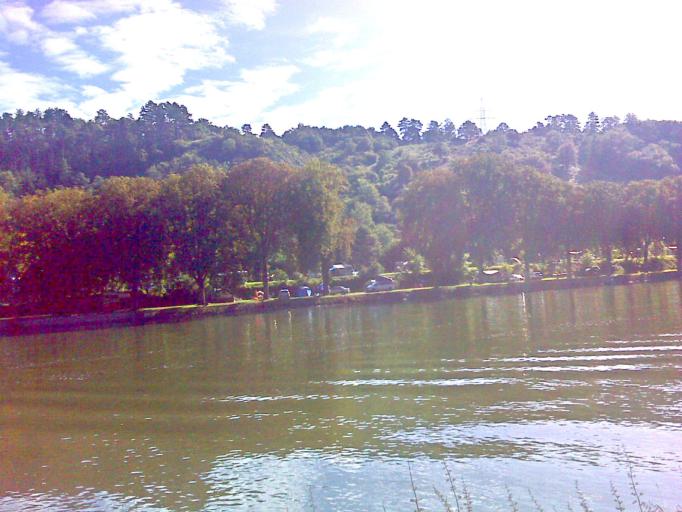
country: BE
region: Wallonia
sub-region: Province de Namur
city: Dinant
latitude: 50.2788
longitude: 4.8936
